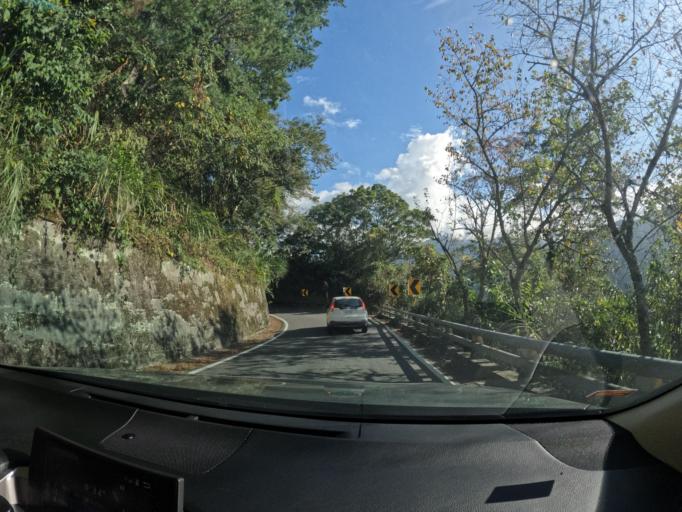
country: TW
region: Taiwan
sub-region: Taitung
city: Taitung
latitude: 23.1924
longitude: 121.0213
